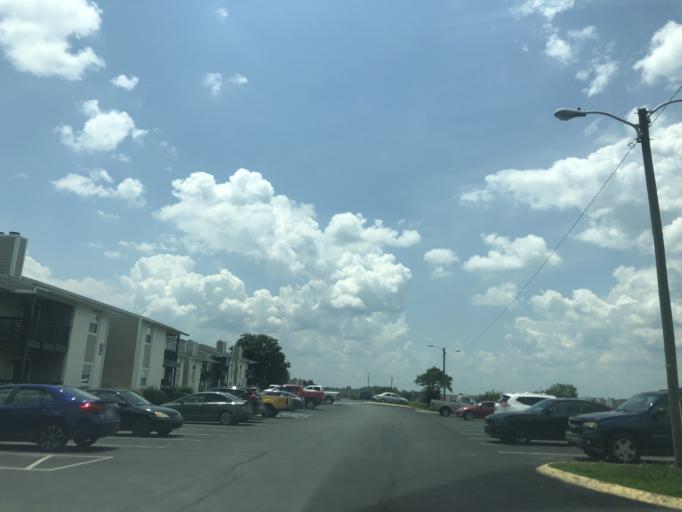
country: US
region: Tennessee
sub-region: Rutherford County
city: La Vergne
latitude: 36.0536
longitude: -86.6596
